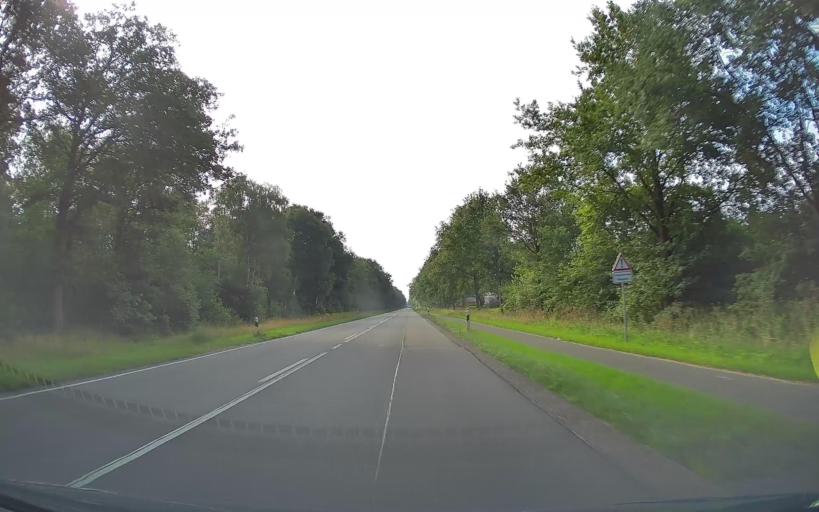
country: DE
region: Lower Saxony
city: Friesoythe
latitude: 52.9996
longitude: 7.8726
